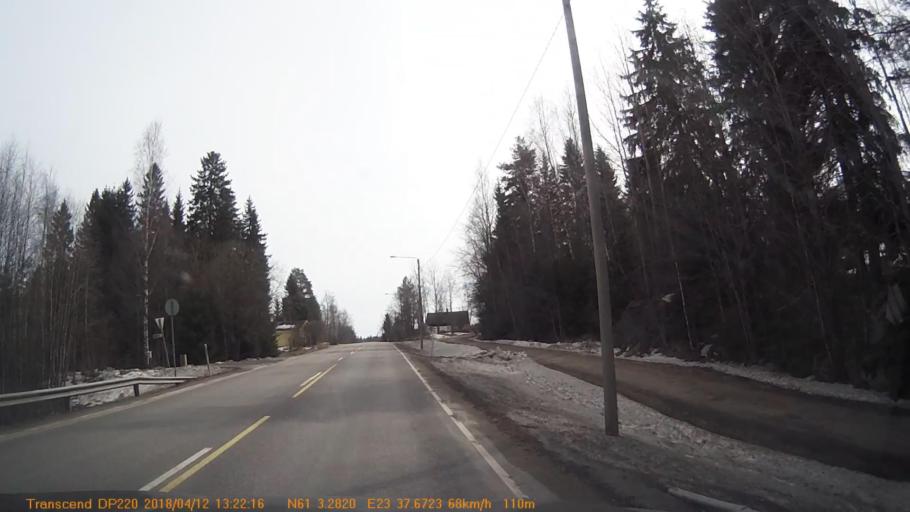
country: FI
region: Pirkanmaa
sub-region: Etelae-Pirkanmaa
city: Urjala
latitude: 61.0538
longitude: 23.6288
